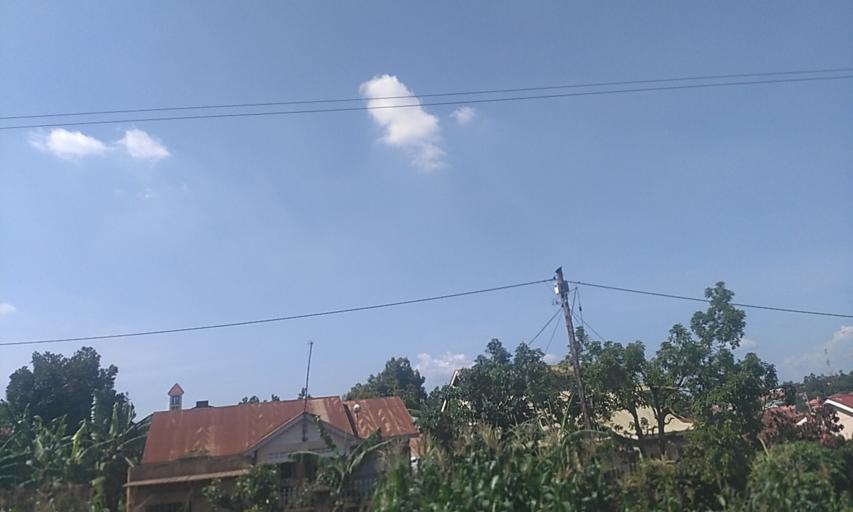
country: UG
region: Central Region
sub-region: Wakiso District
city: Kireka
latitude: 0.3664
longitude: 32.6439
